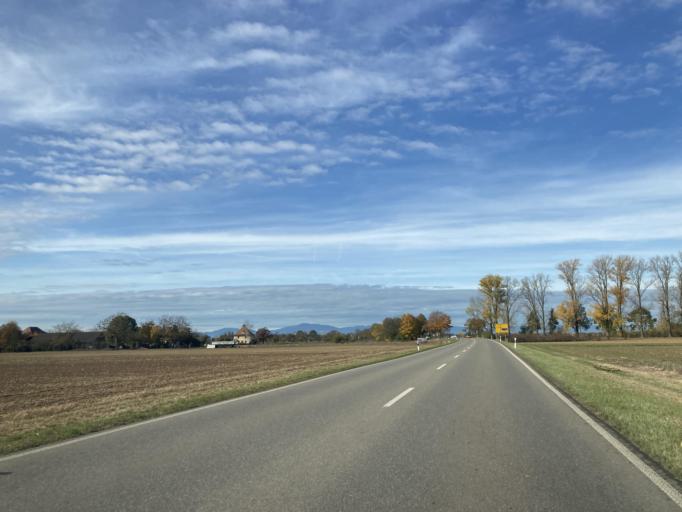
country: DE
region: Baden-Wuerttemberg
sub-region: Freiburg Region
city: Neuenburg am Rhein
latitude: 47.8091
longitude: 7.5870
